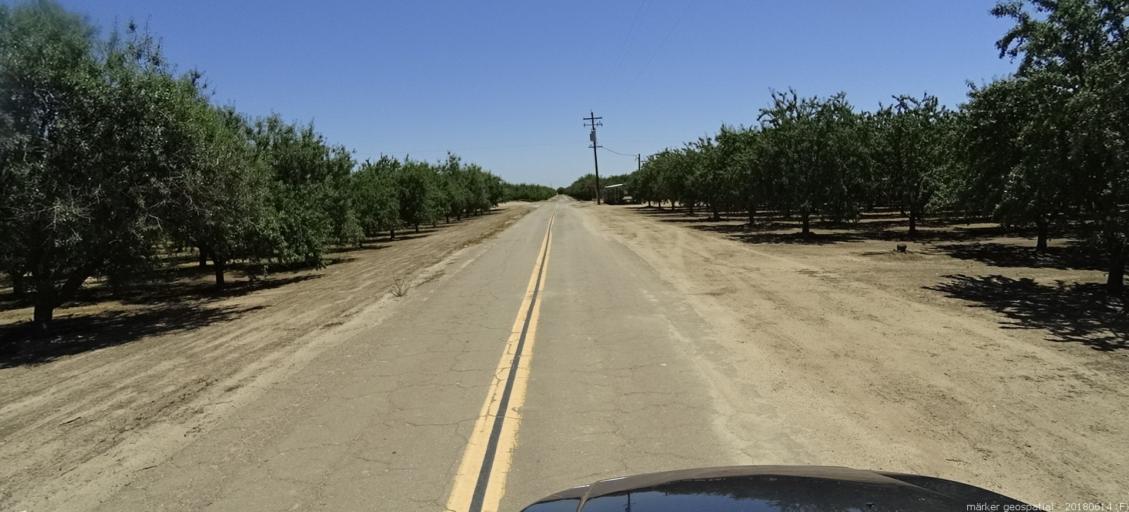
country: US
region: California
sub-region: Madera County
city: Fairmead
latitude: 37.0474
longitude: -120.1945
